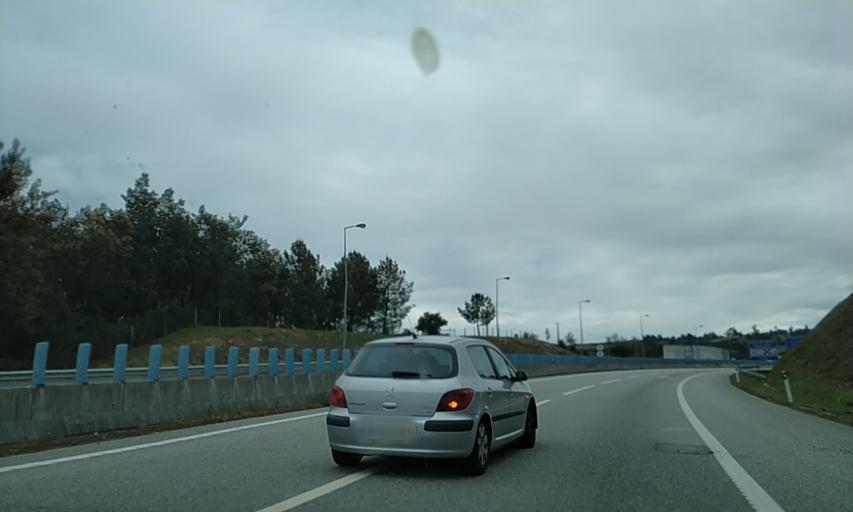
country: PT
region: Viseu
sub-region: Mangualde
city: Mangualde
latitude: 40.6314
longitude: -7.8049
